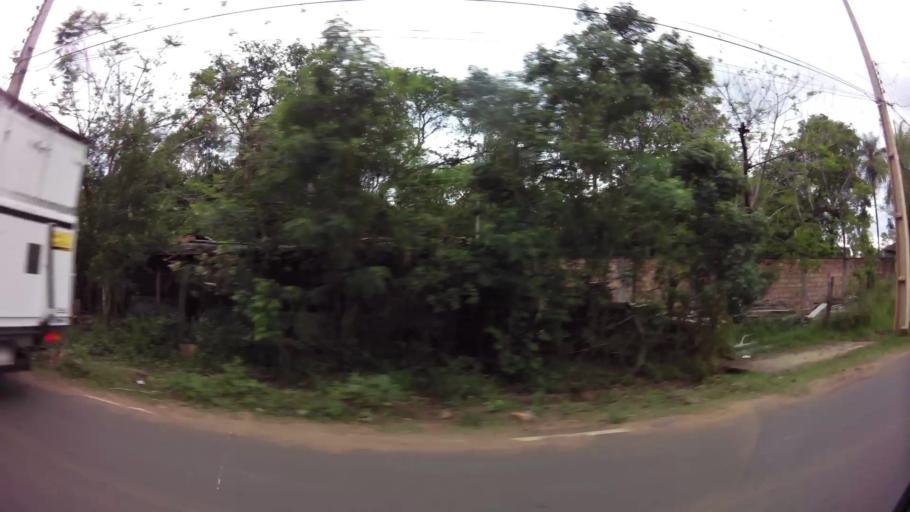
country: PY
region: Central
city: San Lorenzo
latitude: -25.2882
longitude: -57.4898
